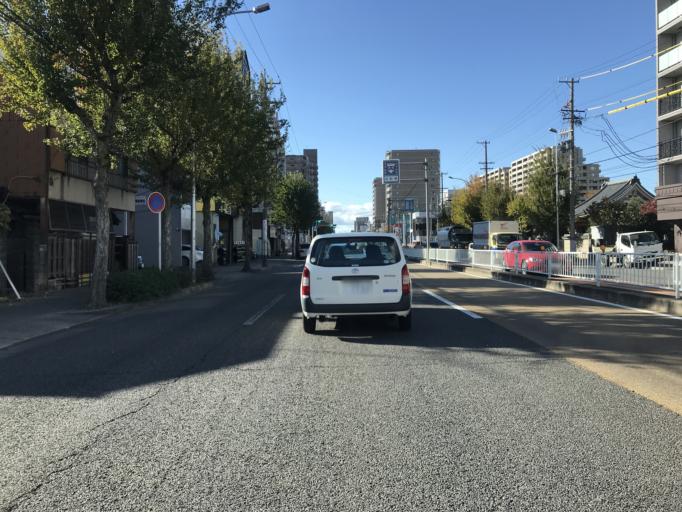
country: JP
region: Aichi
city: Nagoya-shi
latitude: 35.1817
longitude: 136.9385
